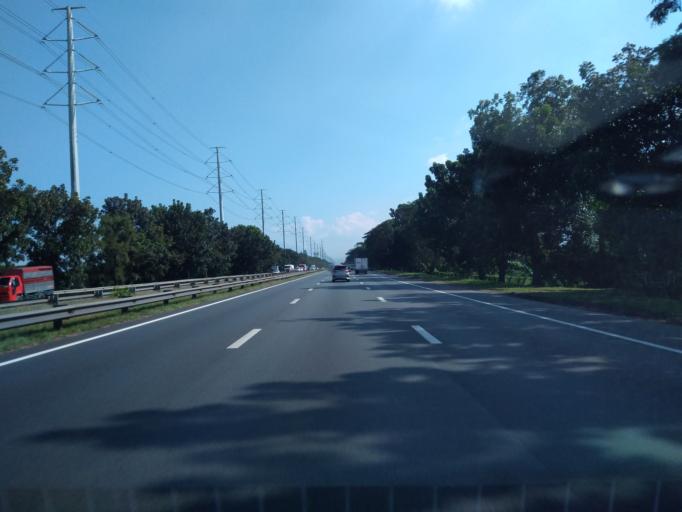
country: PH
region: Calabarzon
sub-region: Province of Laguna
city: Pulong Santa Cruz
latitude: 14.2756
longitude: 121.0934
